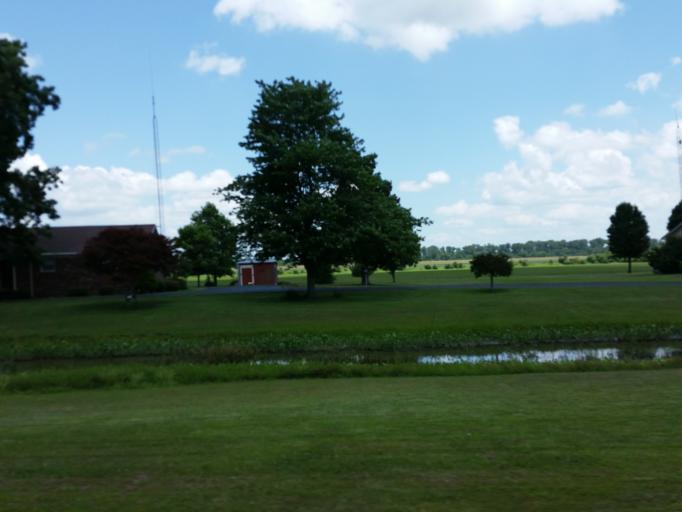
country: US
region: Kentucky
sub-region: Fulton County
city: Hickman
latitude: 36.5493
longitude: -89.2673
